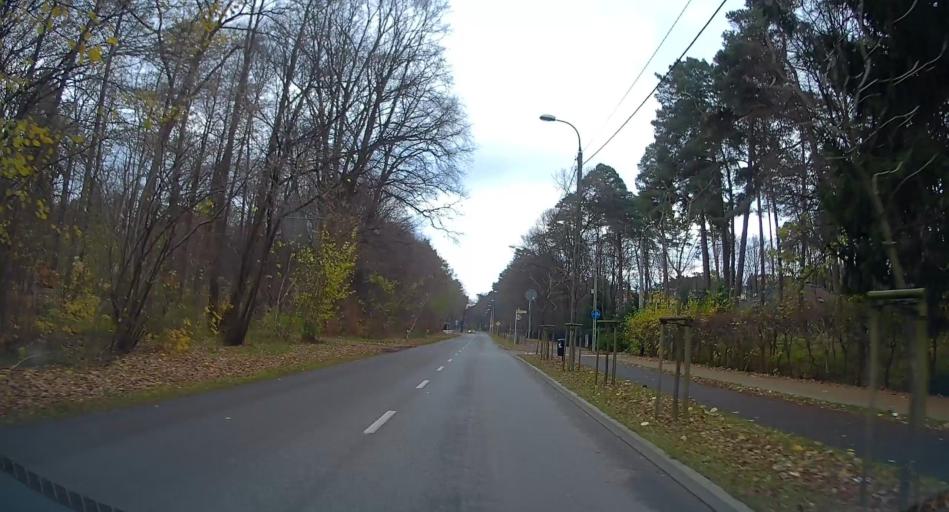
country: PL
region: Masovian Voivodeship
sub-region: Powiat piaseczynski
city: Piaseczno
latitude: 52.0599
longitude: 21.0129
